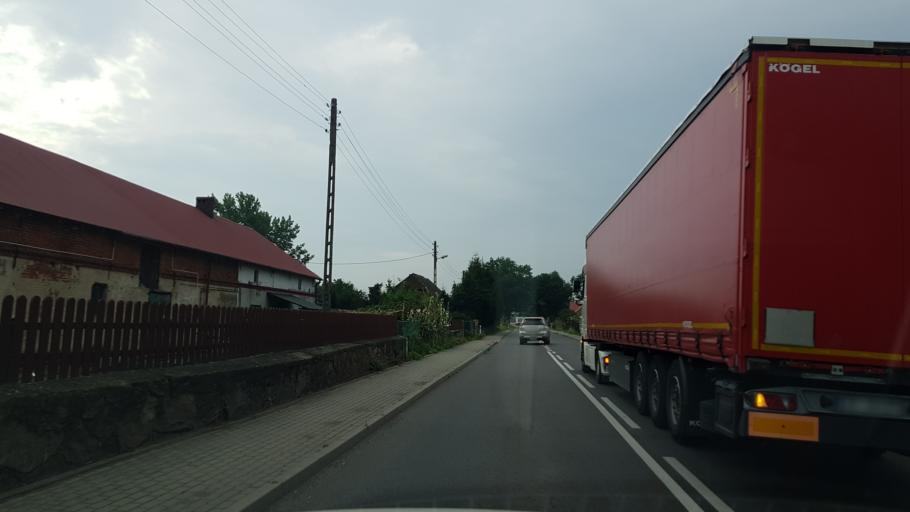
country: PL
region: West Pomeranian Voivodeship
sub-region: Powiat goleniowski
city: Maszewo
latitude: 53.4486
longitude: 15.0646
